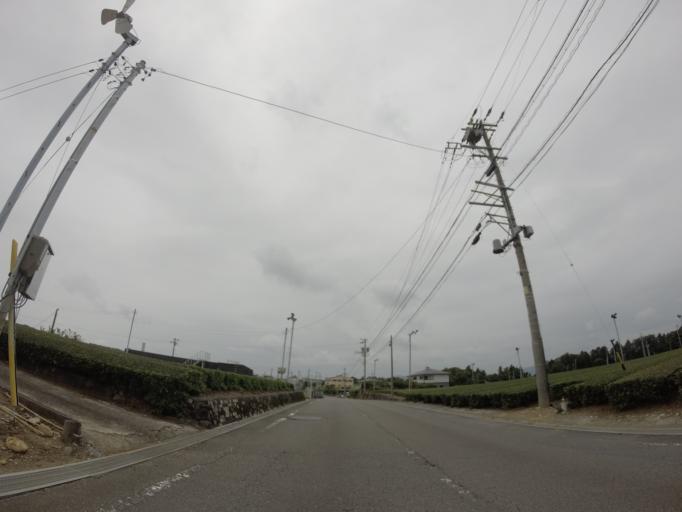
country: JP
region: Shizuoka
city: Kanaya
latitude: 34.8135
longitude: 138.1499
